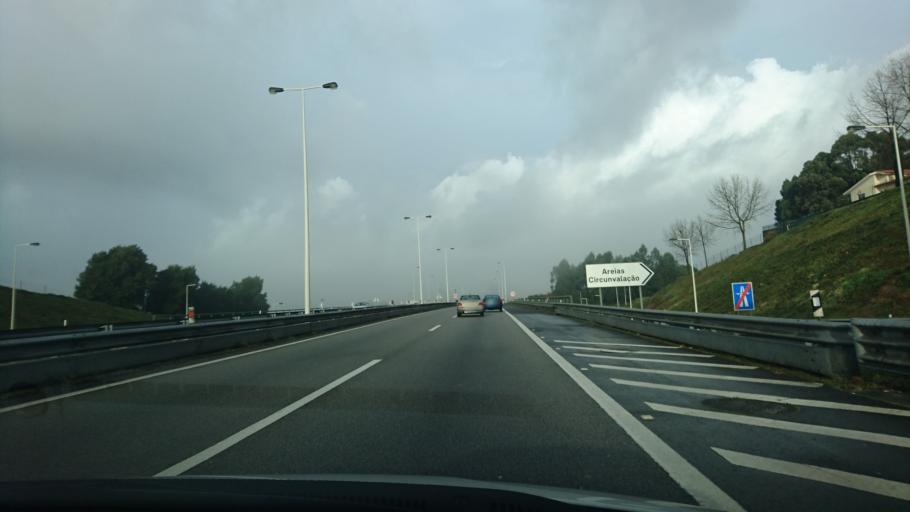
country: PT
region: Porto
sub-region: Gondomar
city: Valbom
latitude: 41.1568
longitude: -8.5597
